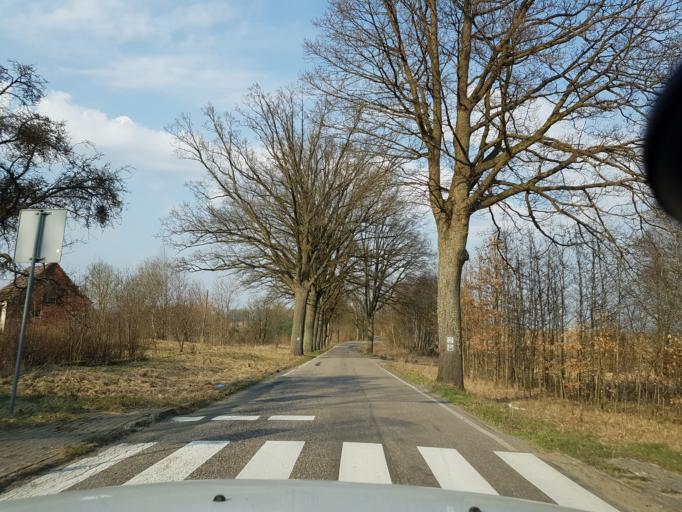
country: PL
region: West Pomeranian Voivodeship
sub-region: Powiat drawski
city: Drawsko Pomorskie
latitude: 53.5987
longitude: 15.9057
